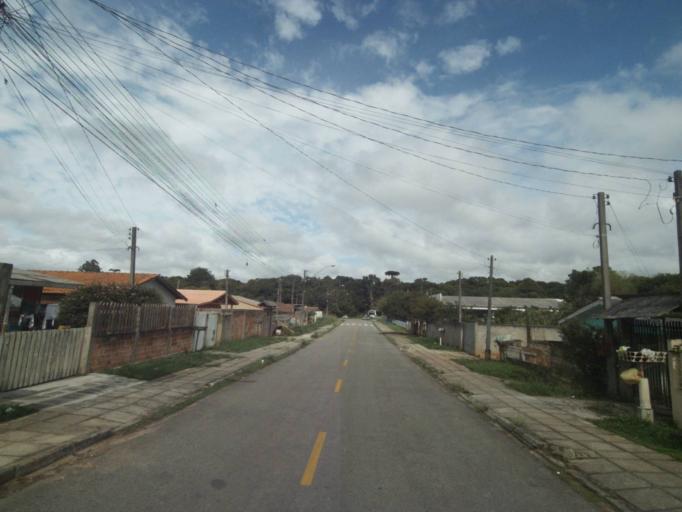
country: BR
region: Parana
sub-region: Quatro Barras
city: Quatro Barras
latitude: -25.3426
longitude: -49.0904
